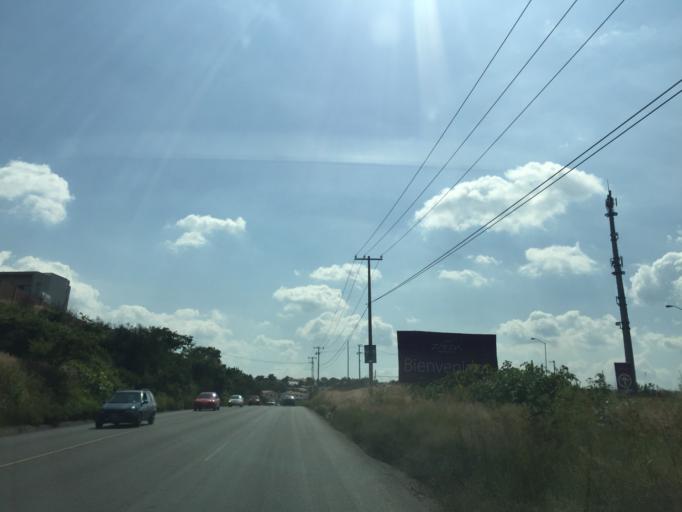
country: MX
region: Guanajuato
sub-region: Leon
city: La Ermita
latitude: 21.1735
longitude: -101.7167
